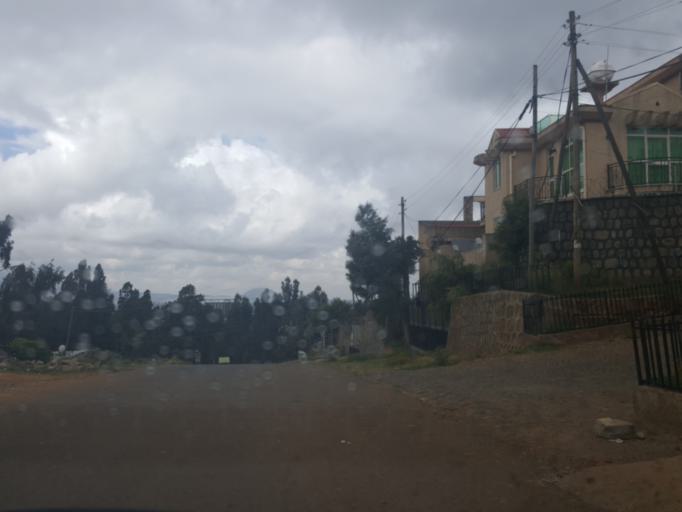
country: ET
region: Adis Abeba
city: Addis Ababa
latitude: 9.0677
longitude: 38.7411
